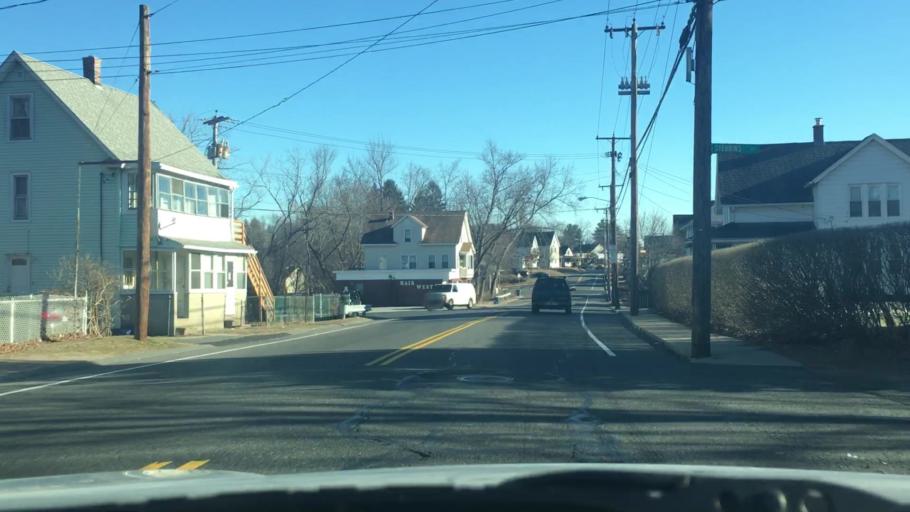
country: US
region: Massachusetts
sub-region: Hampden County
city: Ludlow
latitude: 42.1656
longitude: -72.4864
